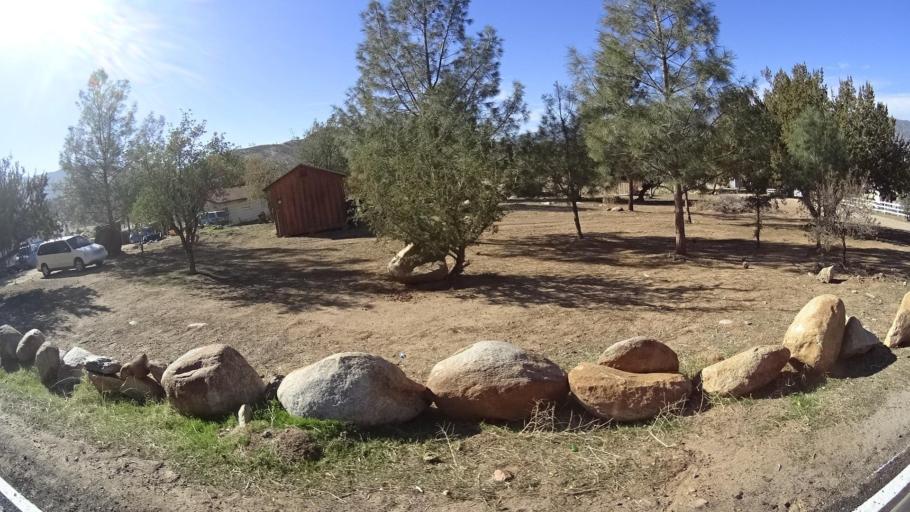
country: US
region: California
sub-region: Kern County
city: Lake Isabella
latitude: 35.6026
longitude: -118.4605
